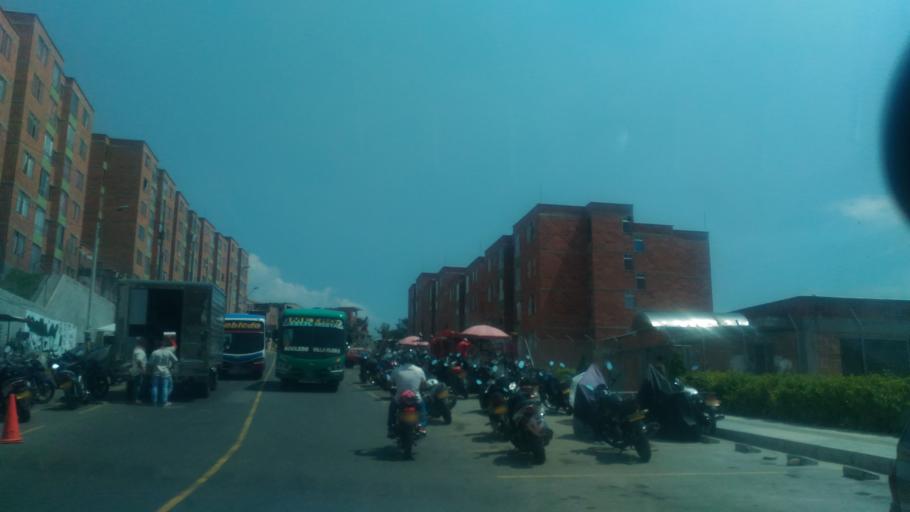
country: CO
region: Antioquia
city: Medellin
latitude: 6.2947
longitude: -75.5873
